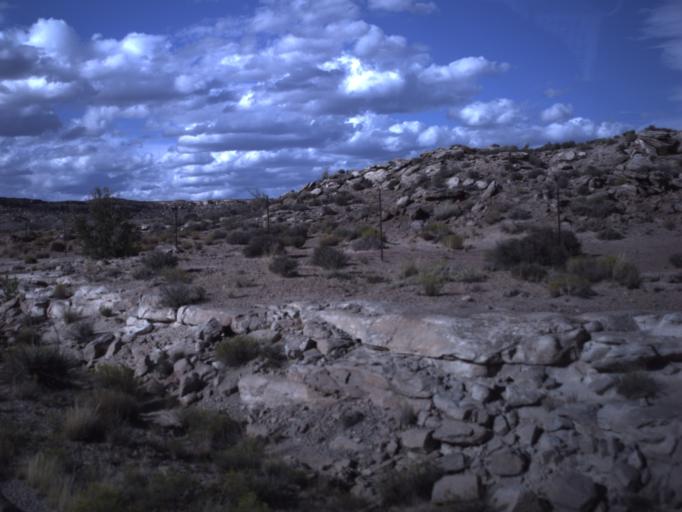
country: US
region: Utah
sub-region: San Juan County
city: Blanding
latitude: 37.3124
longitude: -109.3039
